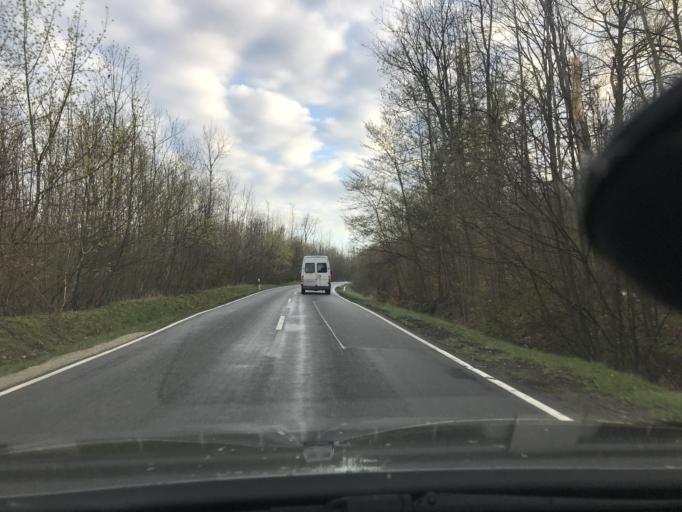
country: DE
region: Thuringia
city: Menteroda
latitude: 51.2927
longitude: 10.5518
